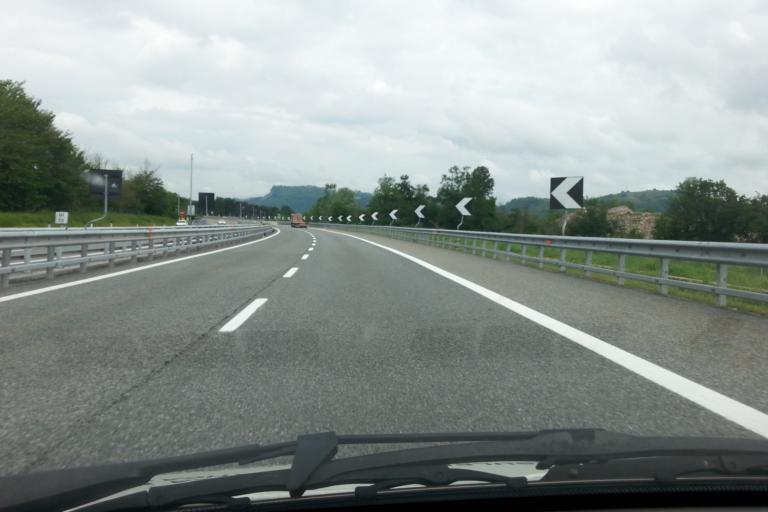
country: IT
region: Piedmont
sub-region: Provincia di Cuneo
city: Lesegno
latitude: 44.4097
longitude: 7.9670
